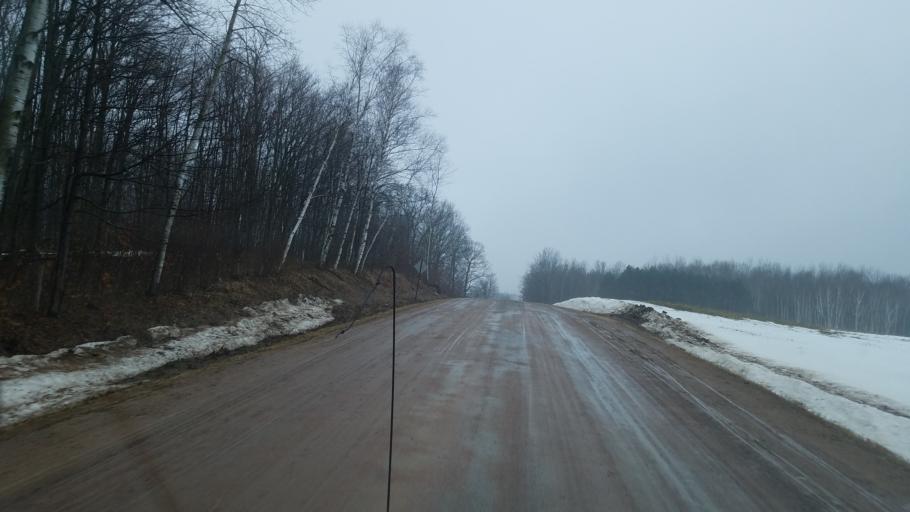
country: US
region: Wisconsin
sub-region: Clark County
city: Loyal
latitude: 44.6101
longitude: -90.3969
